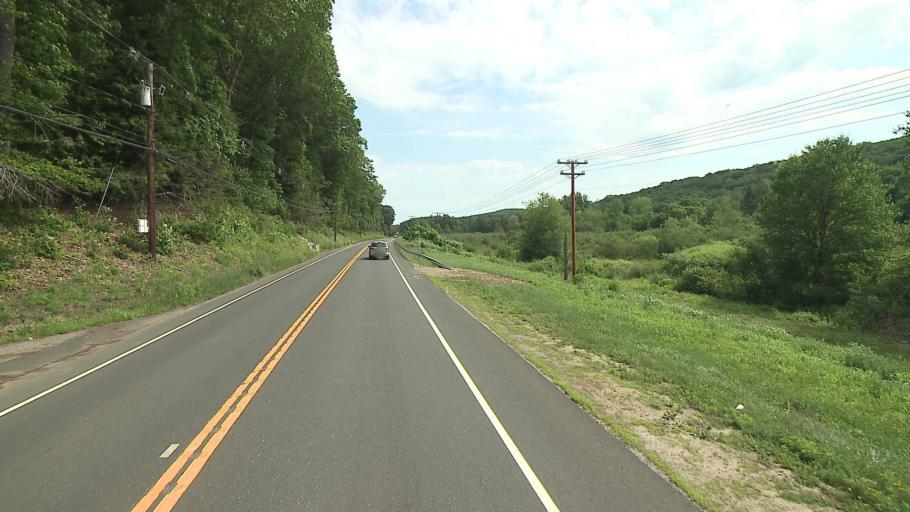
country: US
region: Connecticut
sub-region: Litchfield County
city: Winsted
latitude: 41.8995
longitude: -73.0717
